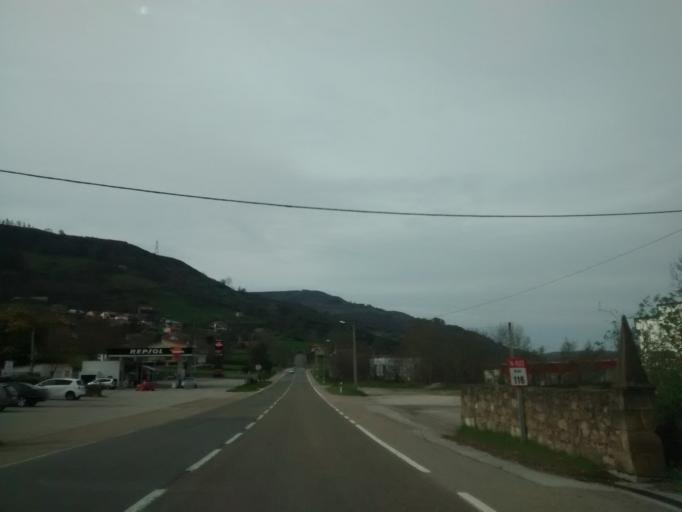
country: ES
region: Cantabria
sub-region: Provincia de Cantabria
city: Santiurde de Toranzo
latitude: 43.2186
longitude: -3.9432
